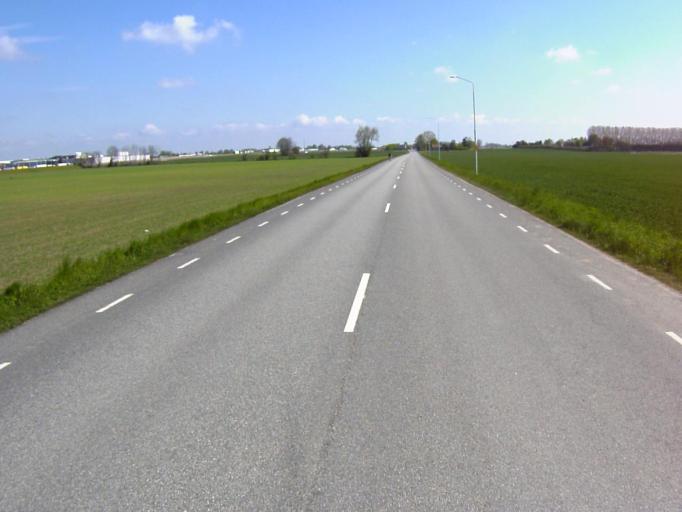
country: SE
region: Skane
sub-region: Kristianstads Kommun
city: Kristianstad
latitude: 56.0186
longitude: 14.2029
